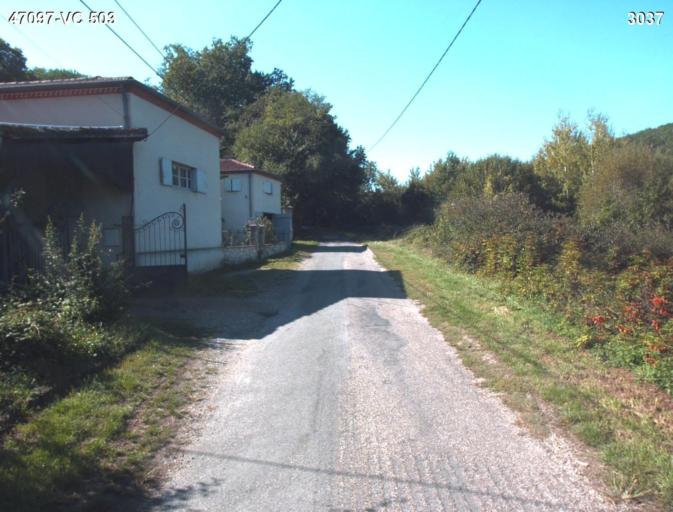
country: FR
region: Aquitaine
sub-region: Departement du Lot-et-Garonne
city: Port-Sainte-Marie
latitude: 44.2157
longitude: 0.3728
